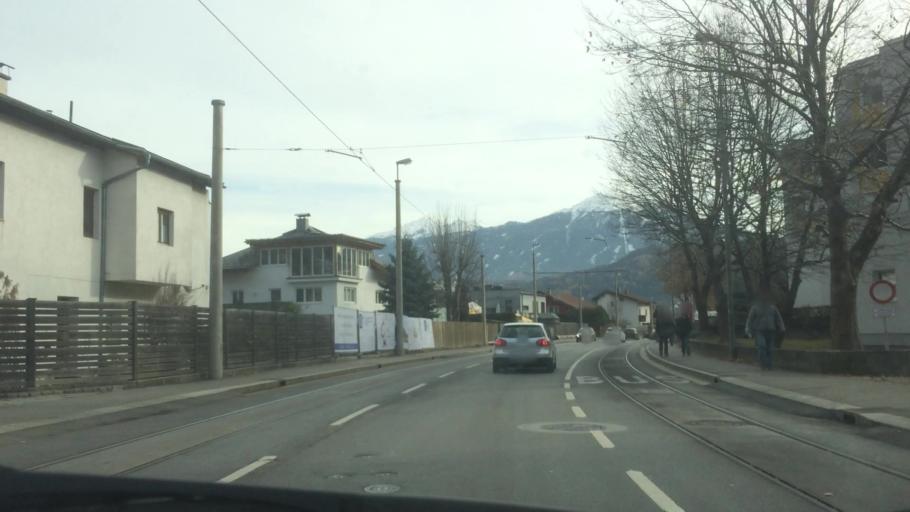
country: AT
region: Tyrol
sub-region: Politischer Bezirk Innsbruck Land
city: Vols
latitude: 47.2649
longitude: 11.3498
